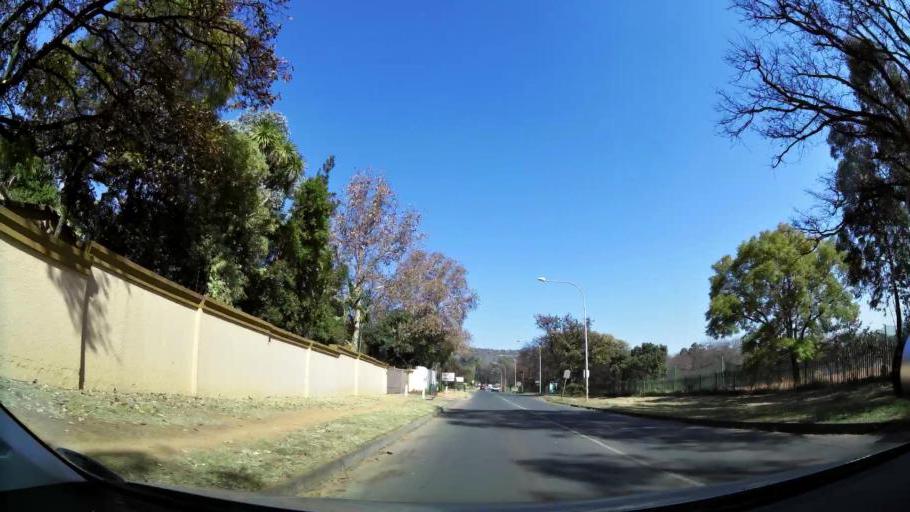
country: ZA
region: Gauteng
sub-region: City of Johannesburg Metropolitan Municipality
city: Modderfontein
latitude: -26.1577
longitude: 28.1191
